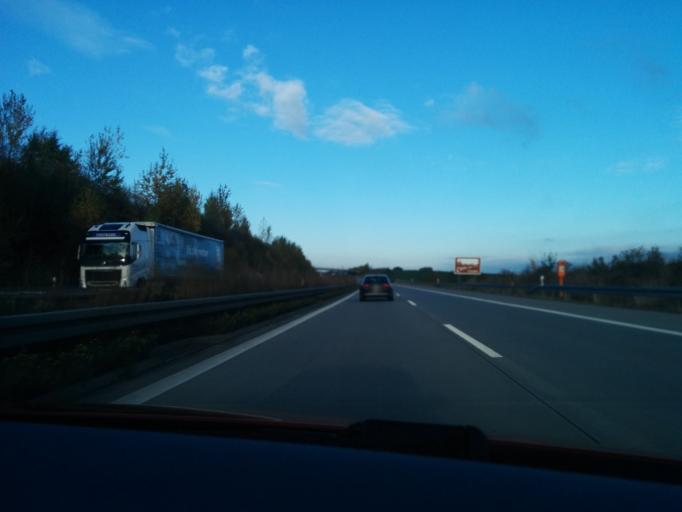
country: DE
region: Saxony
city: Kreischa
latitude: 50.9831
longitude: 13.7869
